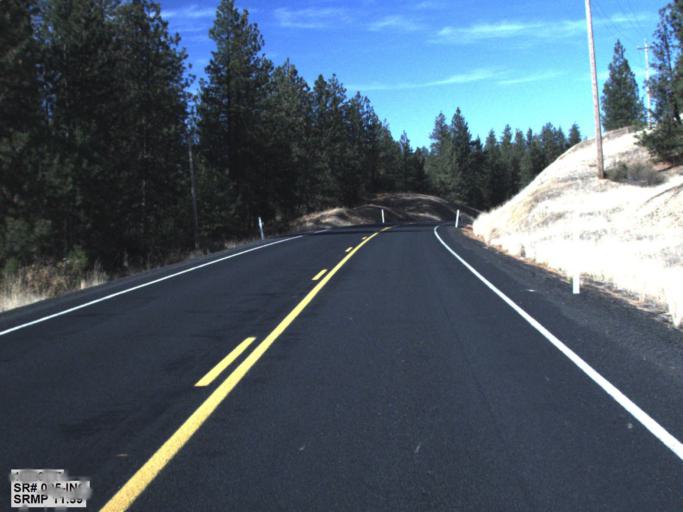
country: US
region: Washington
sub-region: Lincoln County
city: Davenport
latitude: 47.8150
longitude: -118.1822
